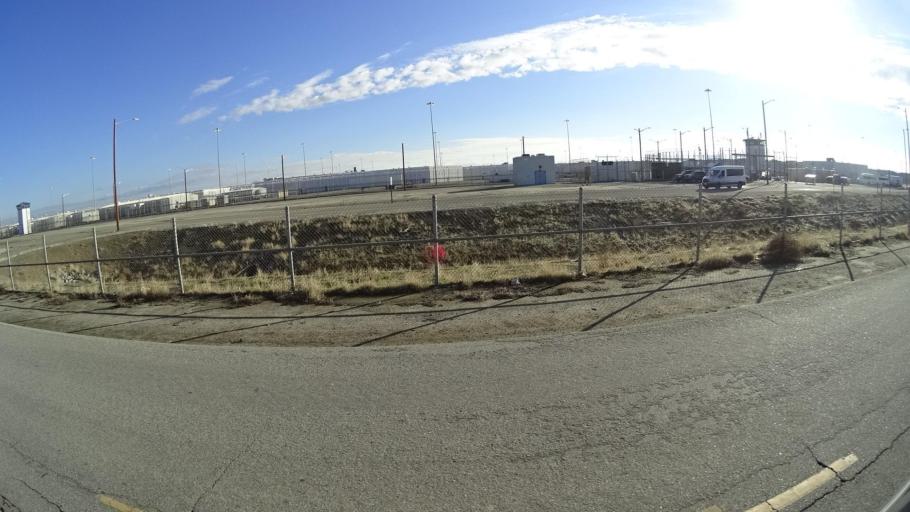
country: US
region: California
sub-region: Kern County
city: Delano
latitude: 35.7671
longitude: -119.3299
